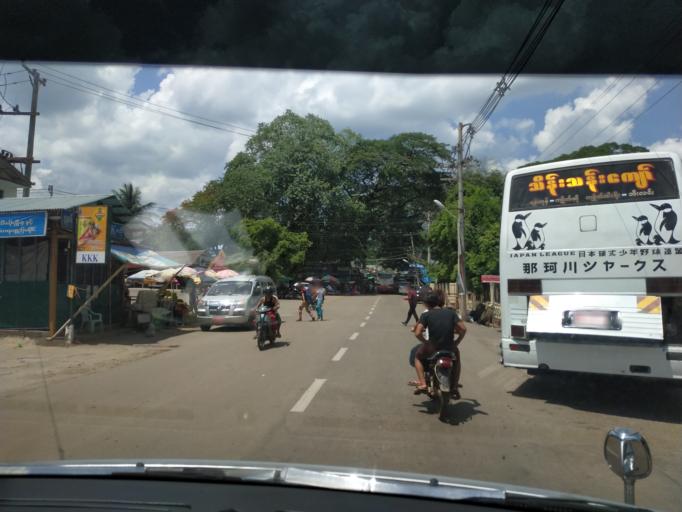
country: MM
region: Mon
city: Kyaikto
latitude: 17.3992
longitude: 97.0780
